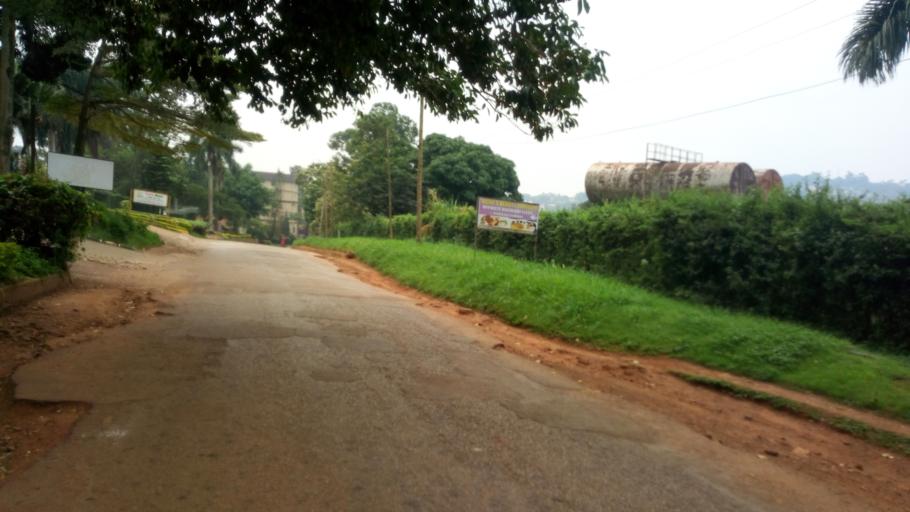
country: UG
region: Central Region
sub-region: Kampala District
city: Kampala
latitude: 0.3141
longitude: 32.6239
